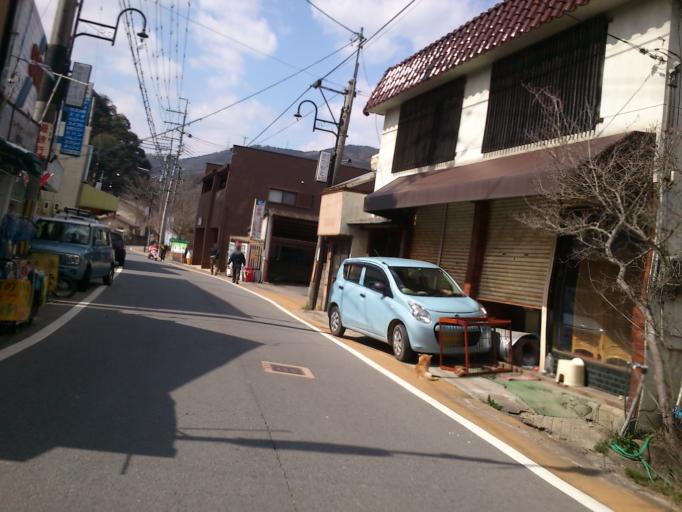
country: JP
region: Nara
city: Nara-shi
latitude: 34.7580
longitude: 135.9356
